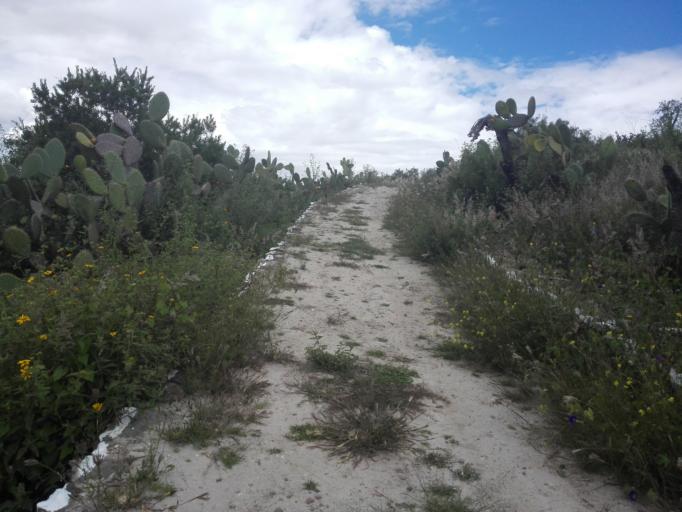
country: PE
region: Ayacucho
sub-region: Provincia de Huamanga
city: Pacaycasa
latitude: -13.0660
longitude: -74.1917
